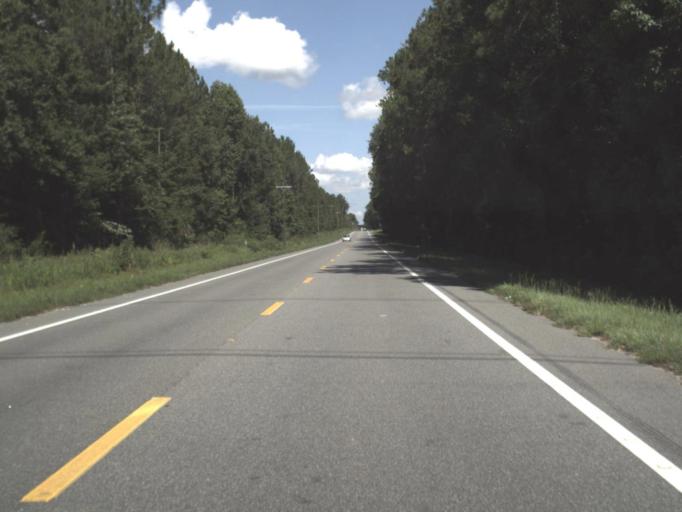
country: US
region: Florida
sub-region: Putnam County
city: Interlachen
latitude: 29.7036
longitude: -81.7760
